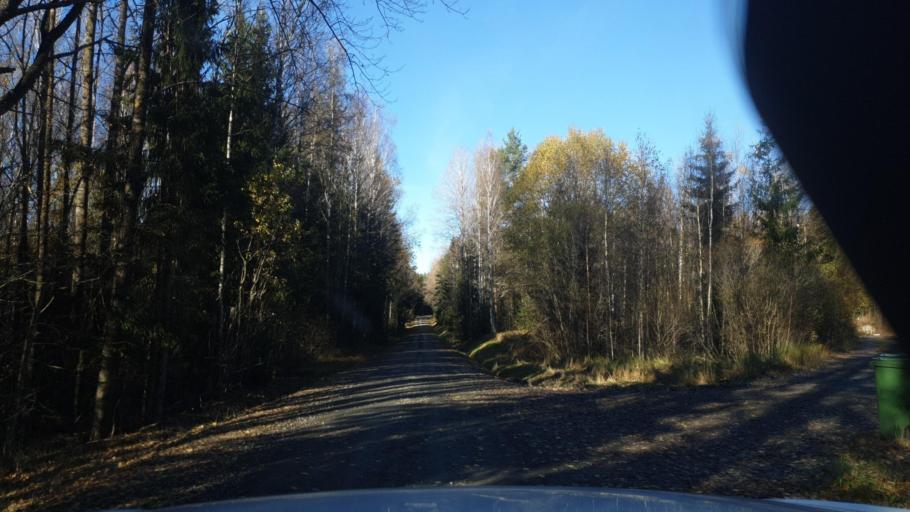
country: SE
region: Vaermland
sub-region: Karlstads Kommun
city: Edsvalla
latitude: 59.5131
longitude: 13.0160
